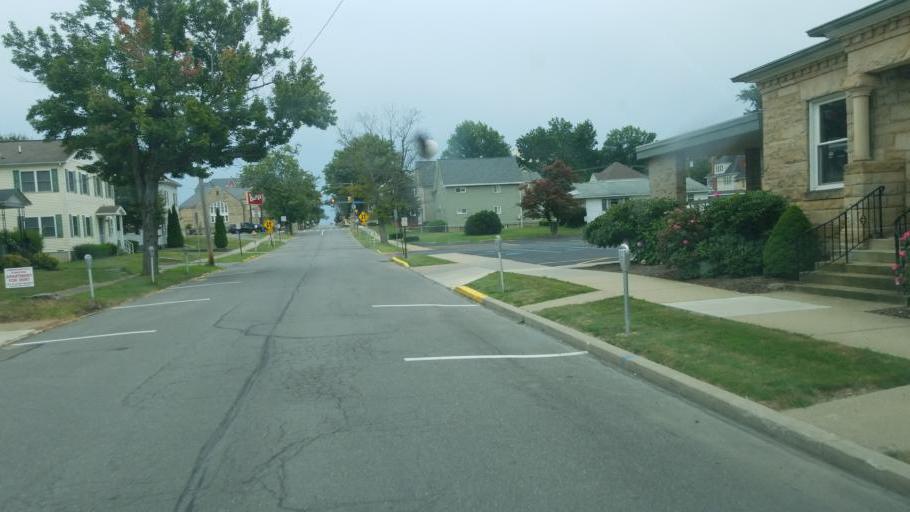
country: US
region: Pennsylvania
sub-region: Clarion County
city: Clarion
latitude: 41.2120
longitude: -79.3825
